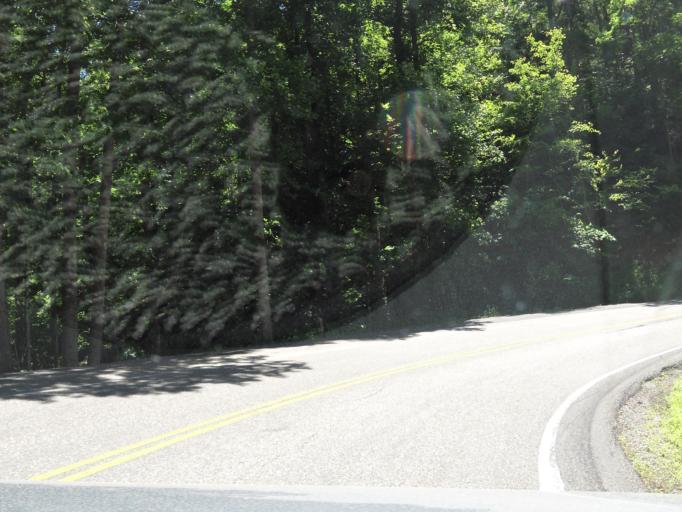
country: US
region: North Carolina
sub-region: Graham County
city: Robbinsville
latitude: 35.5078
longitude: -83.9491
